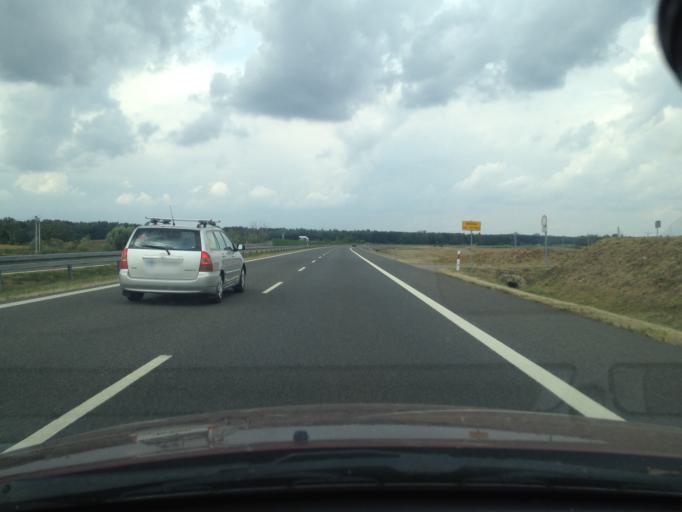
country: PL
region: West Pomeranian Voivodeship
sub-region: Powiat mysliborski
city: Mysliborz
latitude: 52.9854
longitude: 14.8788
